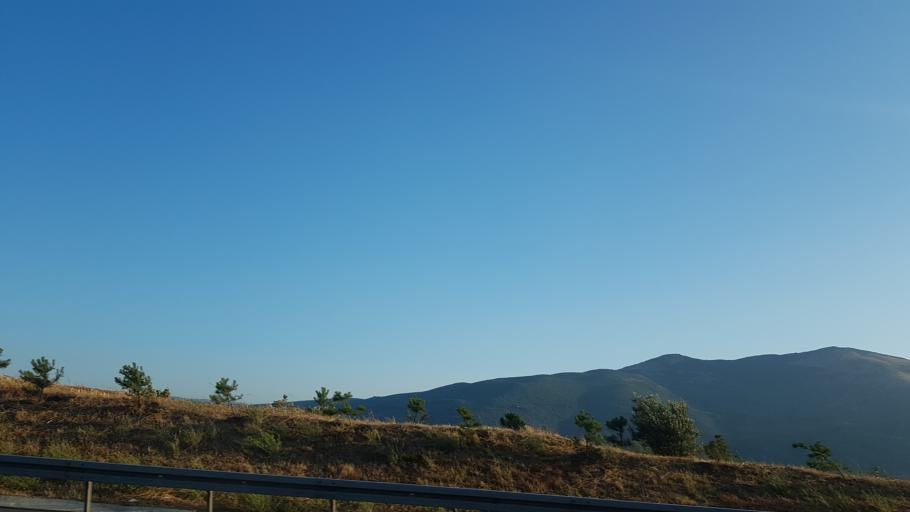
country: TR
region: Bursa
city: Gemlik
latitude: 40.4189
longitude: 29.1585
